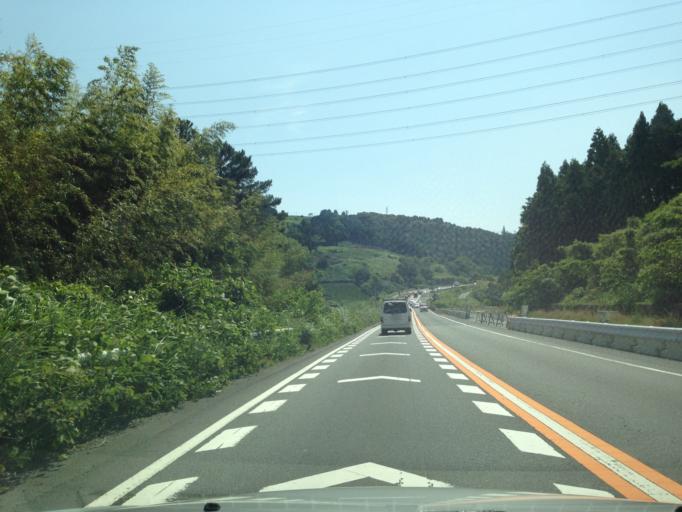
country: JP
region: Shizuoka
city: Kanaya
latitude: 34.8211
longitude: 138.1036
